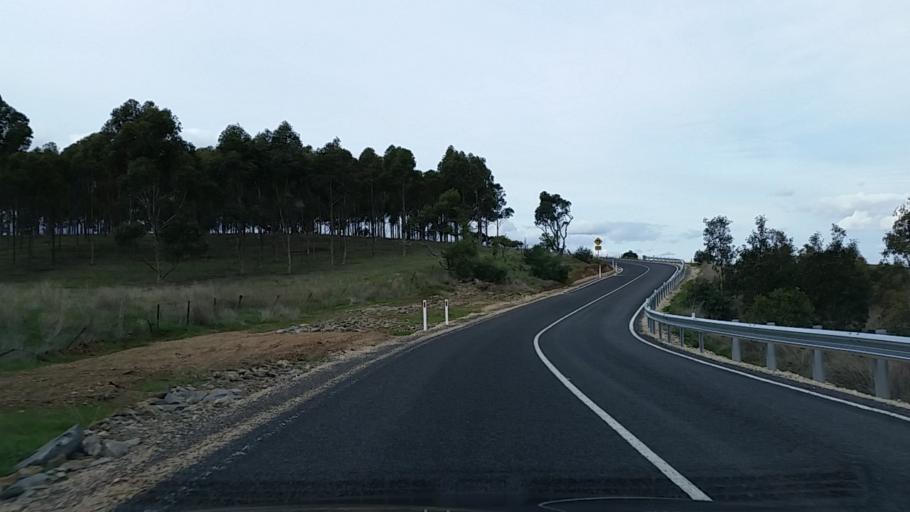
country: AU
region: South Australia
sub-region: Mount Barker
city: Callington
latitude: -35.0114
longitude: 139.0621
